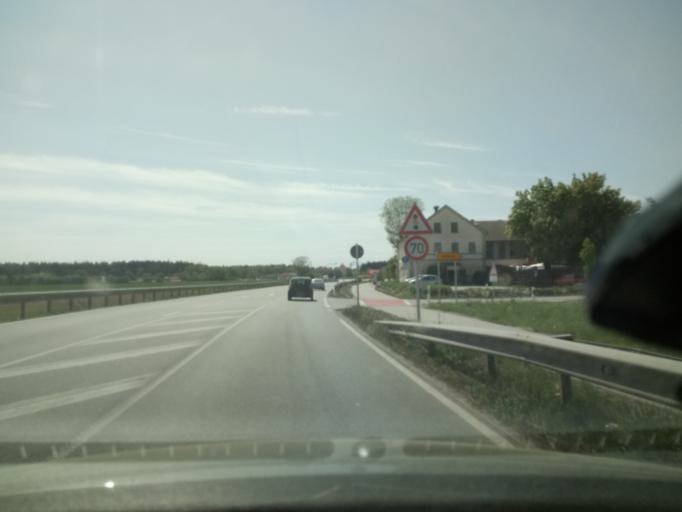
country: DE
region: Bavaria
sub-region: Upper Bavaria
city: Ampfing
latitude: 48.2403
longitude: 12.4123
